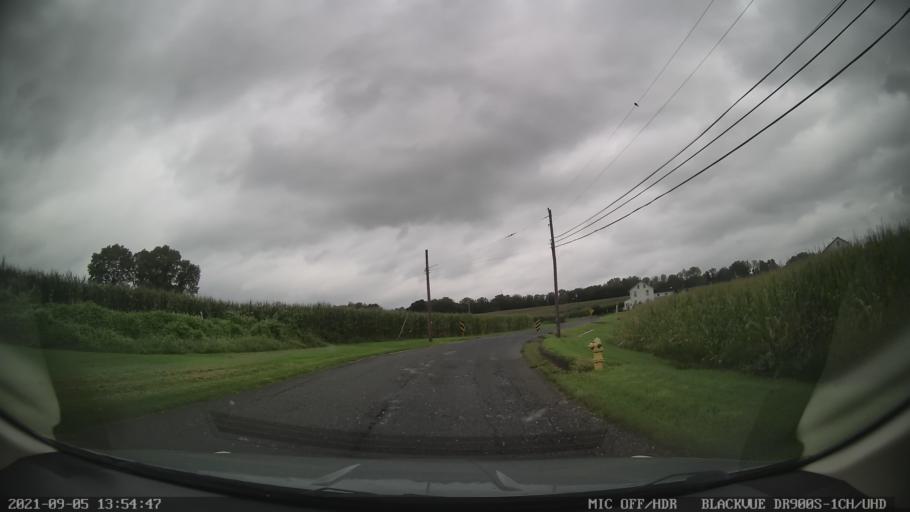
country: US
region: Pennsylvania
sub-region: Lehigh County
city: Stiles
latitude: 40.6519
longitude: -75.5245
